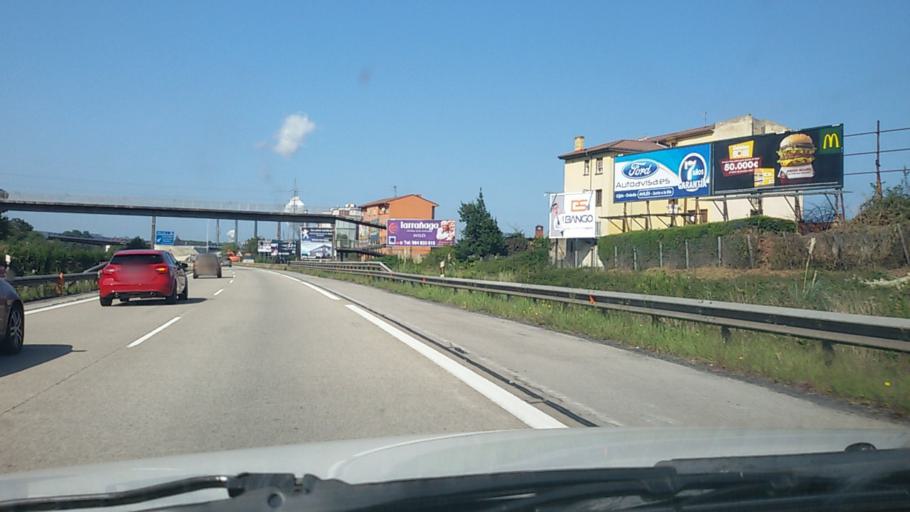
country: ES
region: Asturias
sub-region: Province of Asturias
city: Aviles
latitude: 43.5532
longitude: -5.8860
